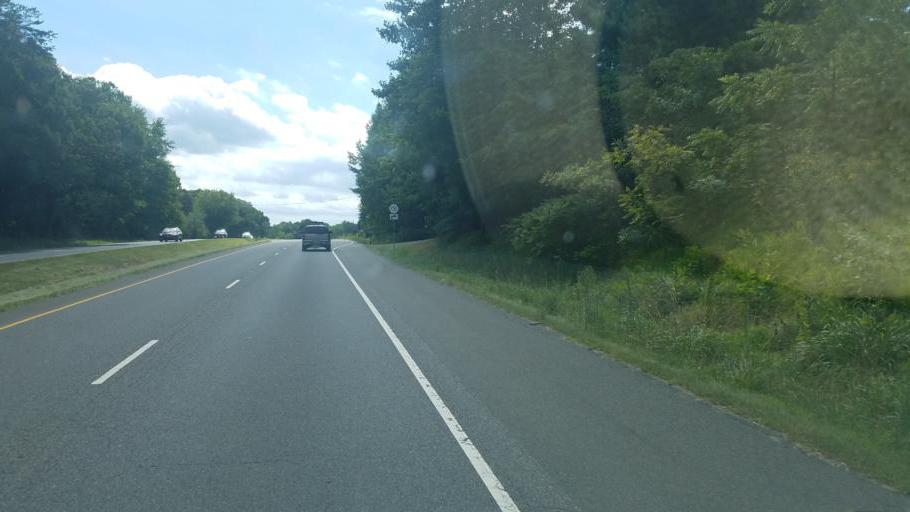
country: US
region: Virginia
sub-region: Stafford County
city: Falmouth
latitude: 38.4030
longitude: -77.5750
